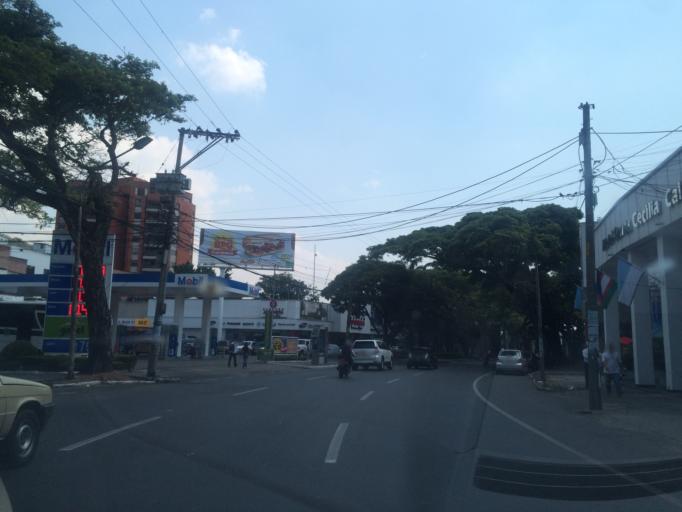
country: CO
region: Valle del Cauca
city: Cali
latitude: 3.4663
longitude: -76.5302
